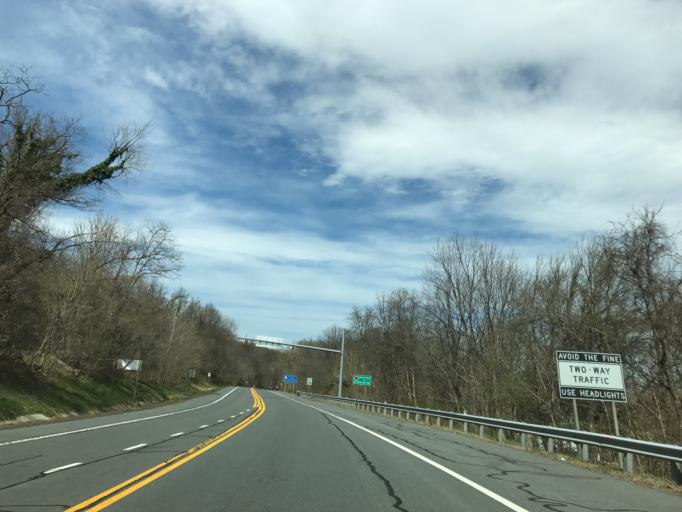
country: US
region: Maryland
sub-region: Frederick County
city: Point of Rocks
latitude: 39.2760
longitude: -77.5406
